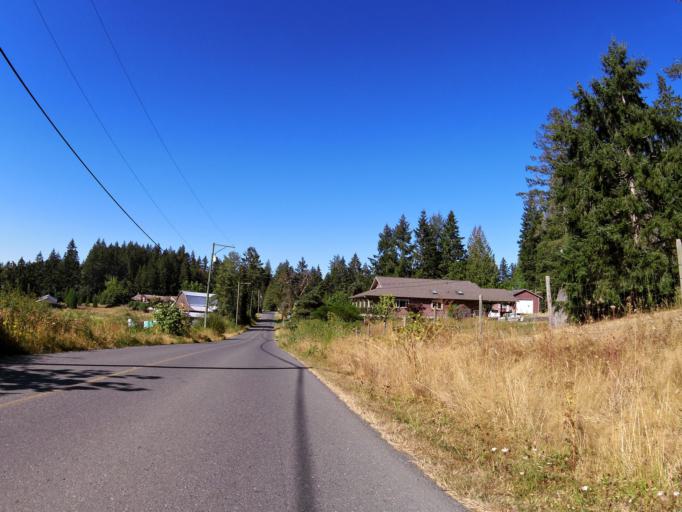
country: CA
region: British Columbia
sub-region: Cowichan Valley Regional District
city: Ladysmith
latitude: 49.0394
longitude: -123.8504
